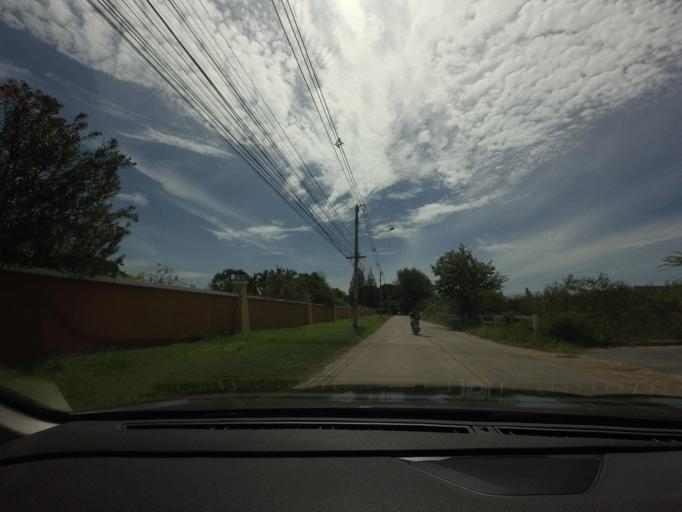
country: TH
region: Prachuap Khiri Khan
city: Hua Hin
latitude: 12.5136
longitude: 99.9702
